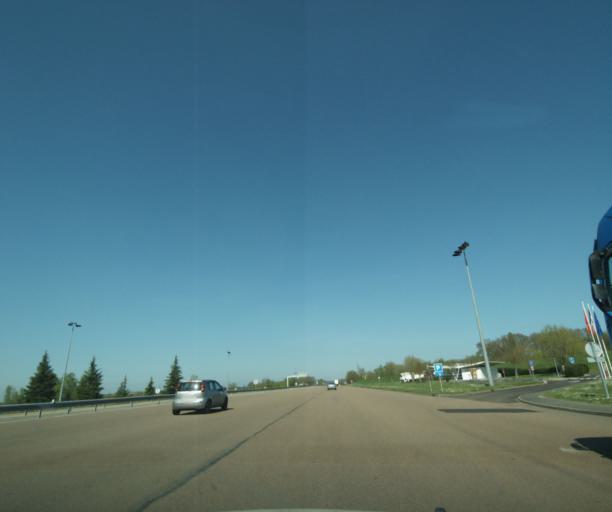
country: FR
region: Bourgogne
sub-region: Departement de la Nievre
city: Cosne-Cours-sur-Loire
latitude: 47.4376
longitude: 2.9411
